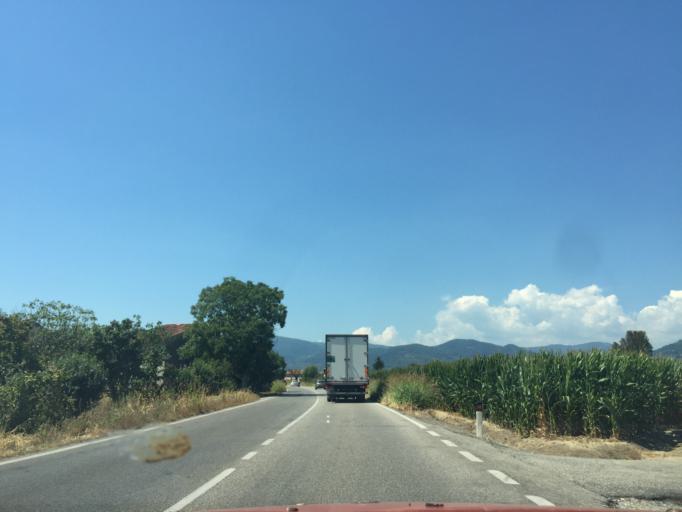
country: IT
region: Tuscany
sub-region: Provincia di Pistoia
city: Chiesina Uzzanese
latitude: 43.8516
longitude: 10.7088
